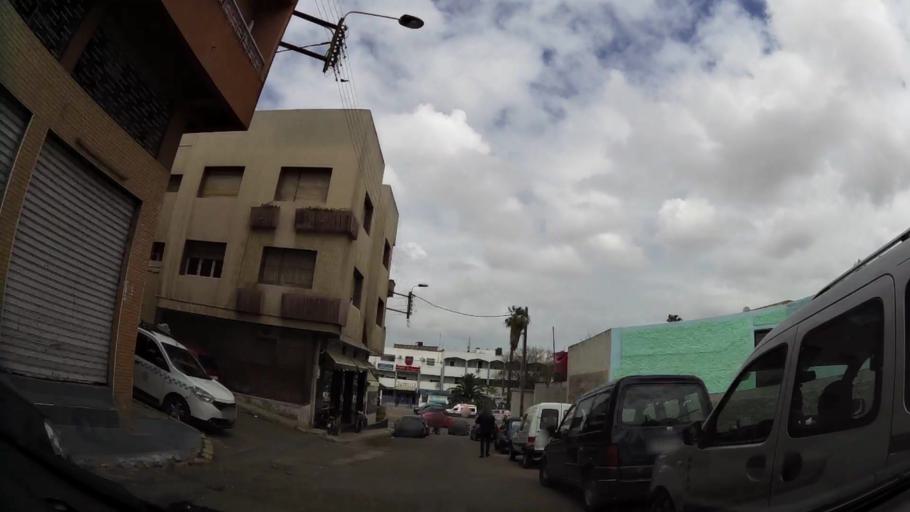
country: MA
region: Grand Casablanca
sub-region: Casablanca
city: Casablanca
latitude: 33.5398
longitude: -7.5972
